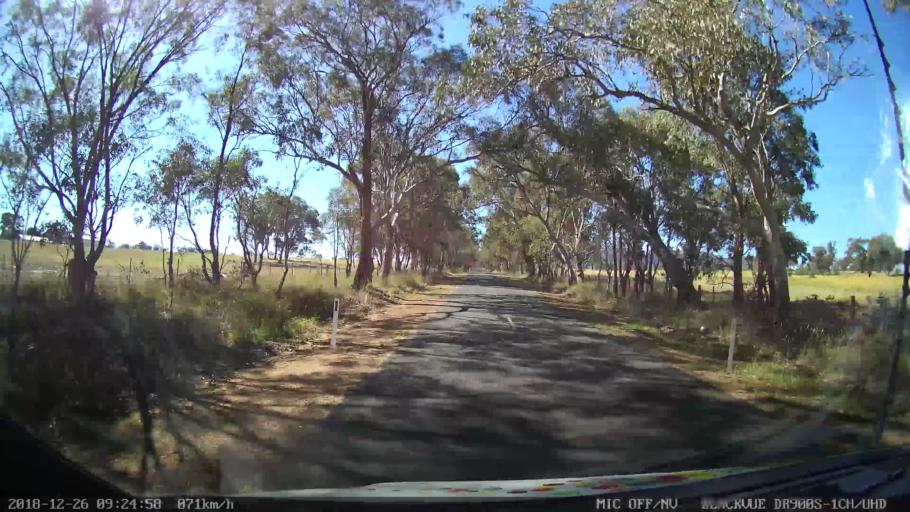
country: AU
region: New South Wales
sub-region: Mid-Western Regional
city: Kandos
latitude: -32.8155
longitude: 150.0017
